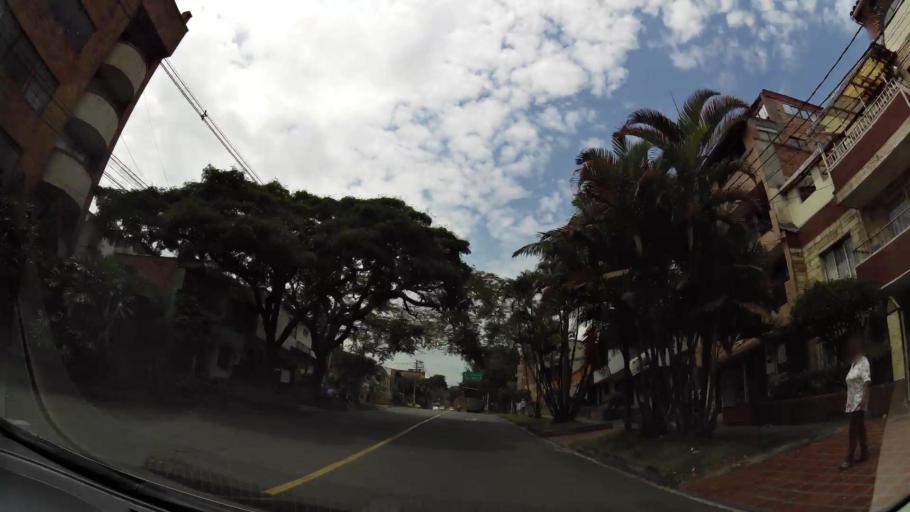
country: CO
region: Antioquia
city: Medellin
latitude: 6.2478
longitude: -75.6150
